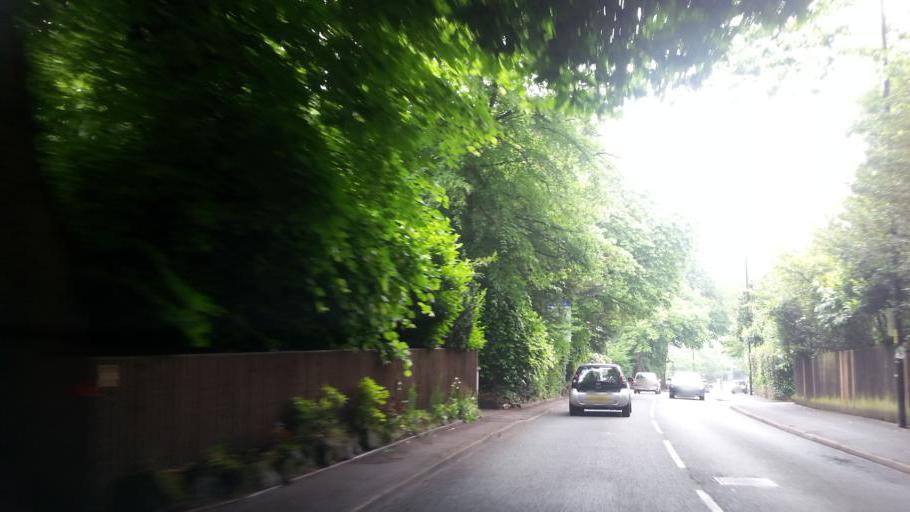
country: GB
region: England
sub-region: City and Borough of Birmingham
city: Sutton Coldfield
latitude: 52.5803
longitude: -1.8307
